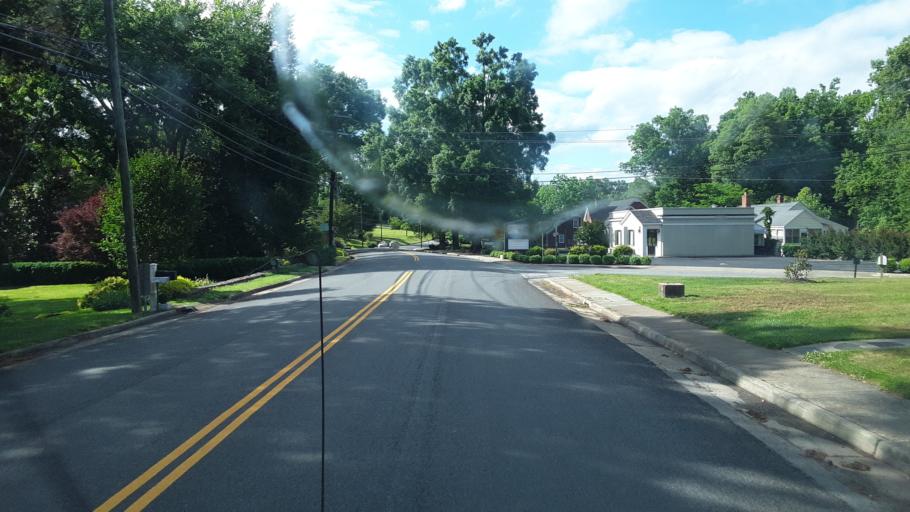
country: US
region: Virginia
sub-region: Pittsylvania County
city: Chatham
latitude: 36.8137
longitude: -79.3949
